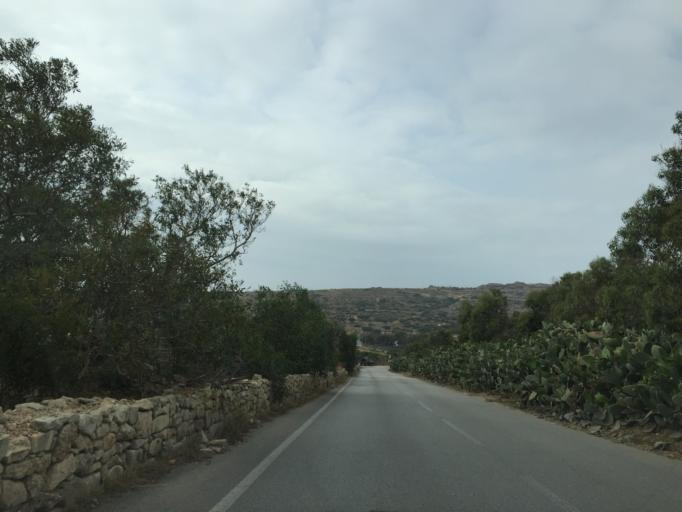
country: MT
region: Il-Mellieha
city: Mellieha
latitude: 35.9432
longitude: 14.3526
